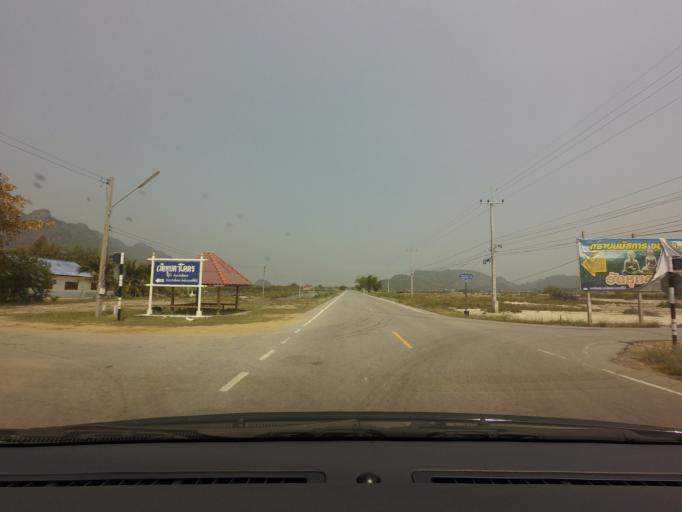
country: TH
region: Prachuap Khiri Khan
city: Sam Roi Yot
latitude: 12.1854
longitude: 99.9763
